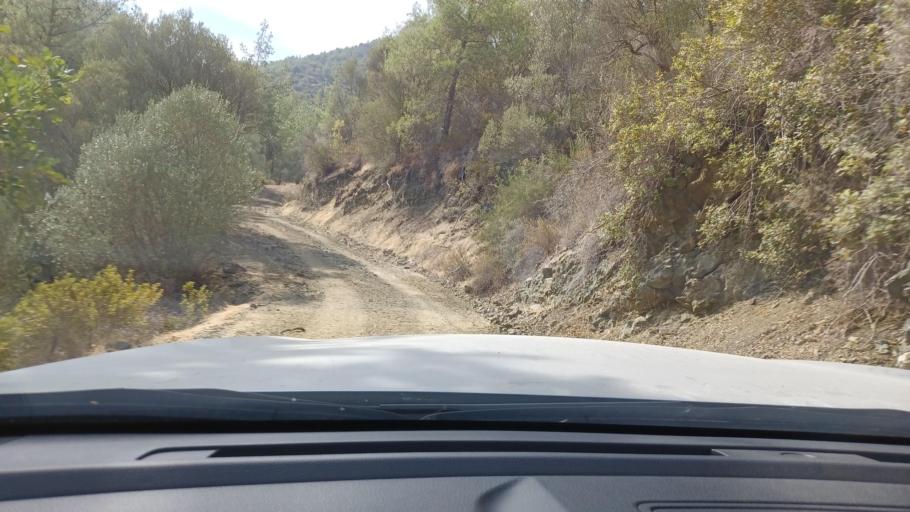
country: CY
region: Pafos
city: Polis
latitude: 35.0165
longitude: 32.5358
